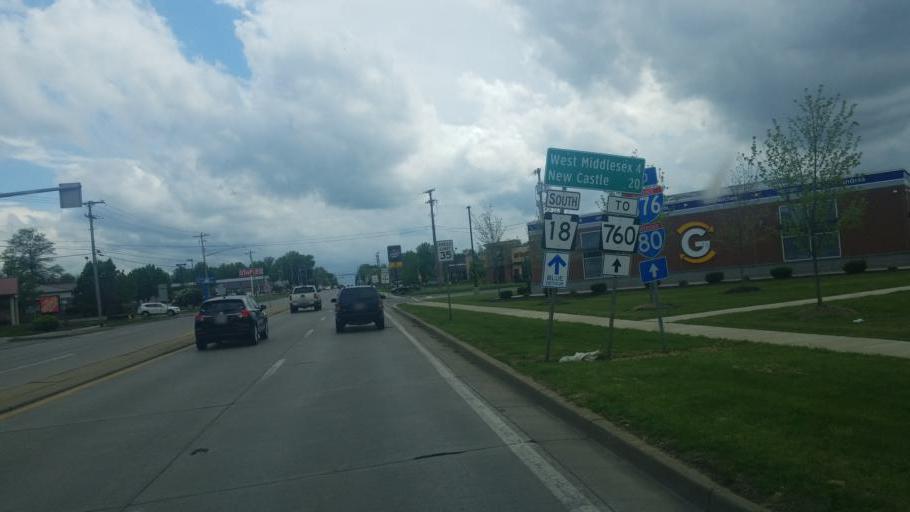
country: US
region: Pennsylvania
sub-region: Mercer County
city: Hermitage
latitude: 41.2290
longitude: -80.4504
